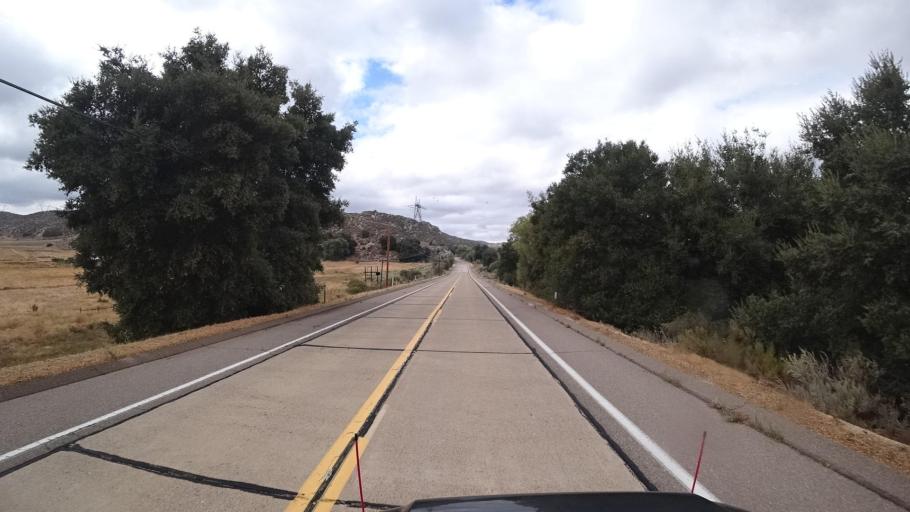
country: US
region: California
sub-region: San Diego County
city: Campo
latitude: 32.7245
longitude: -116.4280
